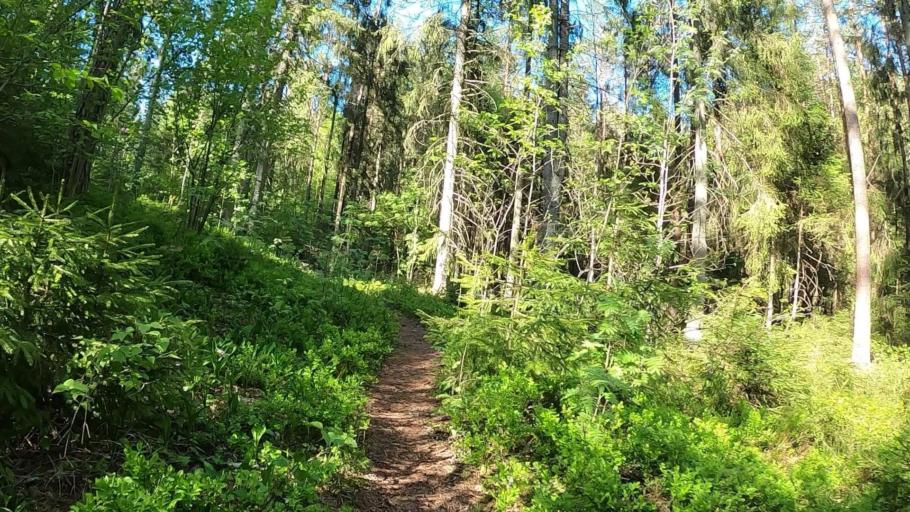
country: LV
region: Baldone
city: Baldone
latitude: 56.7738
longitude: 24.4117
